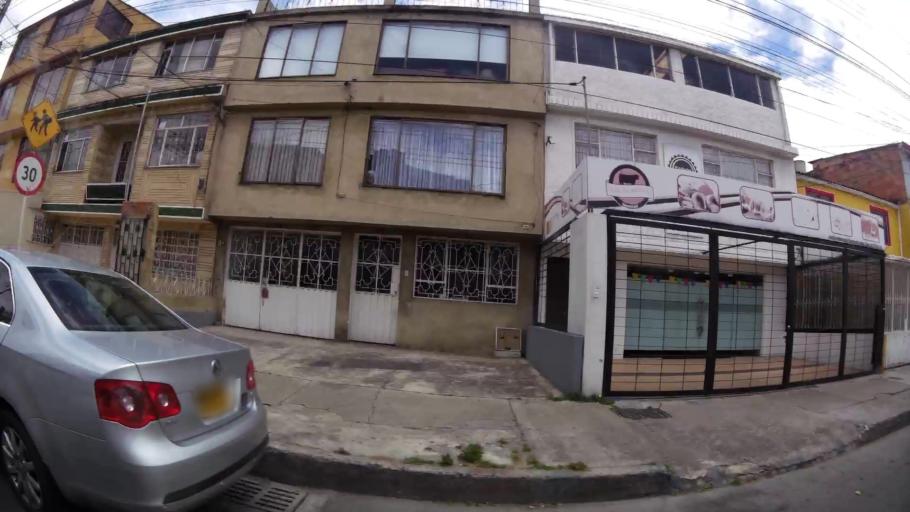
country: CO
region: Bogota D.C.
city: Bogota
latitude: 4.6034
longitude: -74.1083
